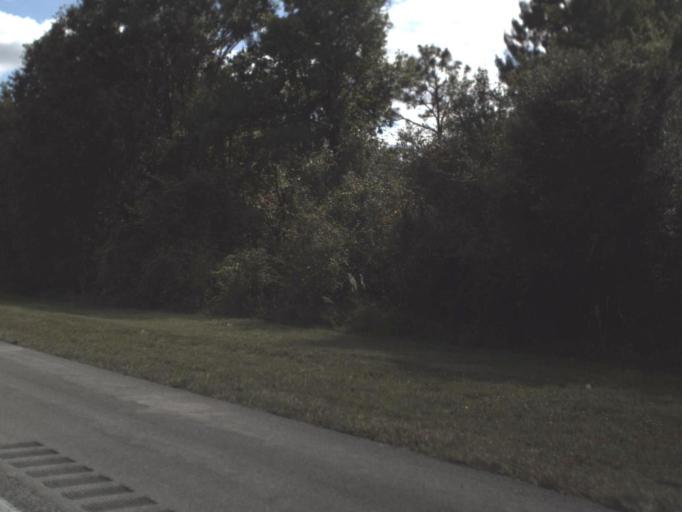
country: US
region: Florida
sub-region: Indian River County
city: Fellsmere
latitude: 27.6158
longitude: -80.8334
